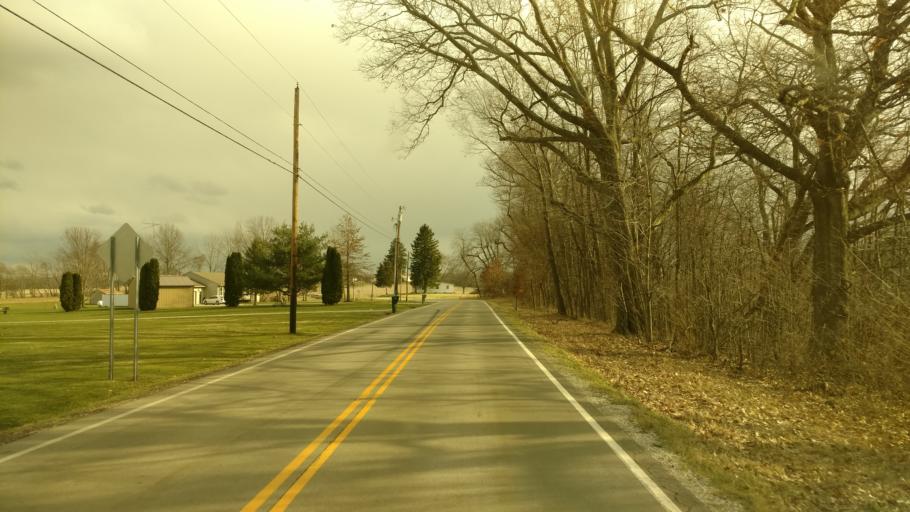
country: US
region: Ohio
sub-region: Crawford County
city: Galion
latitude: 40.7265
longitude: -82.7403
